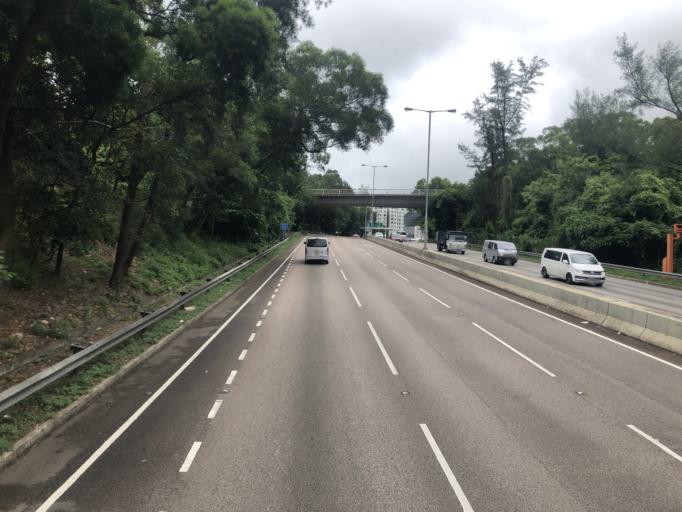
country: HK
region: Wanchai
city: Wan Chai
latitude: 22.2807
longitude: 114.2356
